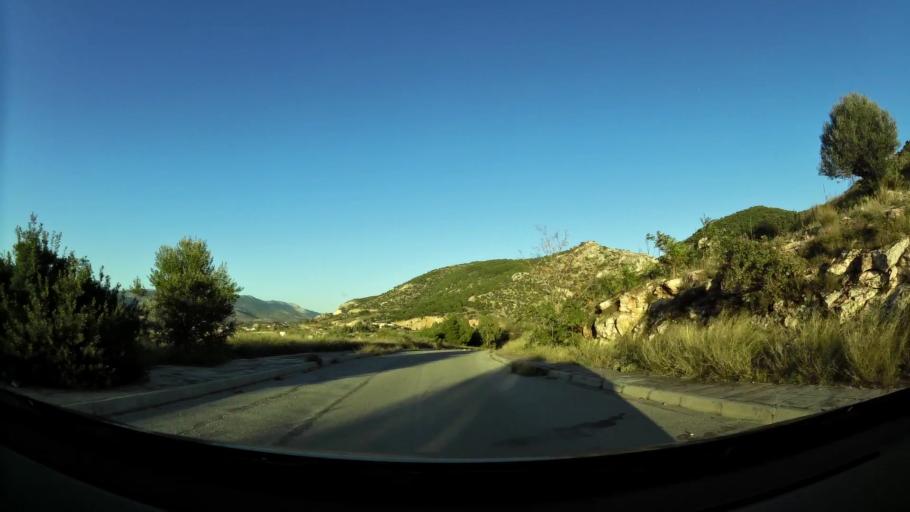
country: GR
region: Attica
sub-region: Nomarchia Athinas
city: Skaramangas
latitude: 38.0324
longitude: 23.6326
